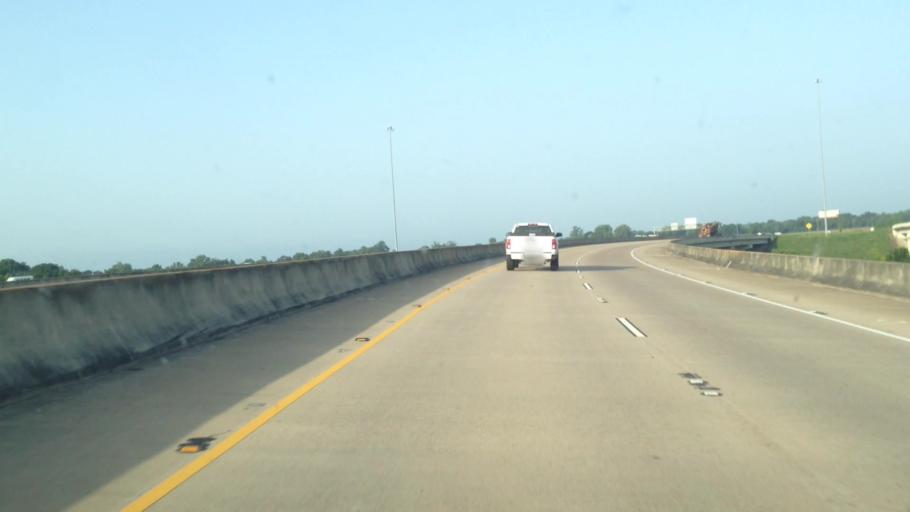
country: US
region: Louisiana
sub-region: Rapides Parish
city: Alexandria
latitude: 31.2428
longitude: -92.4306
